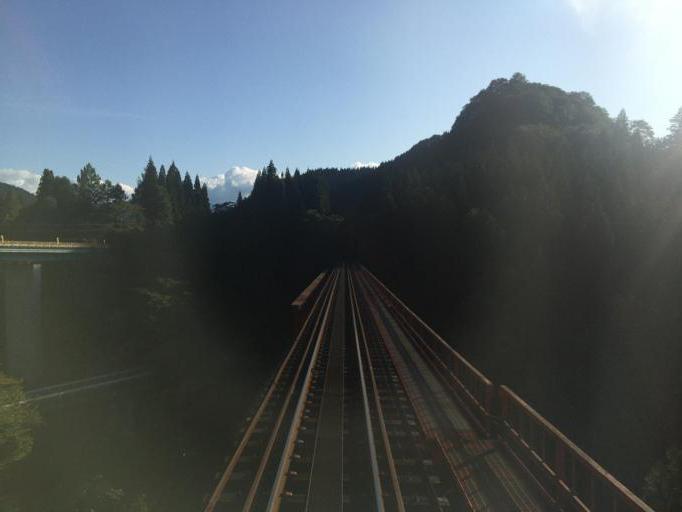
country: JP
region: Akita
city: Takanosu
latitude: 39.9536
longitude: 140.4154
